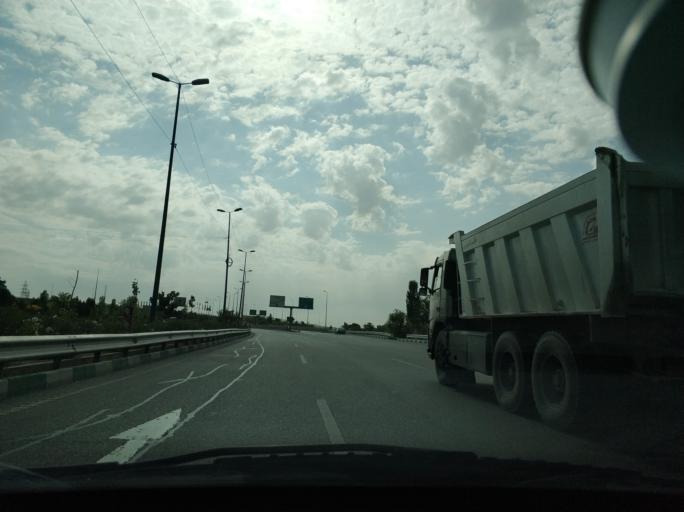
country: IR
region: Tehran
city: Tehran
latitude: 35.7237
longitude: 51.5824
